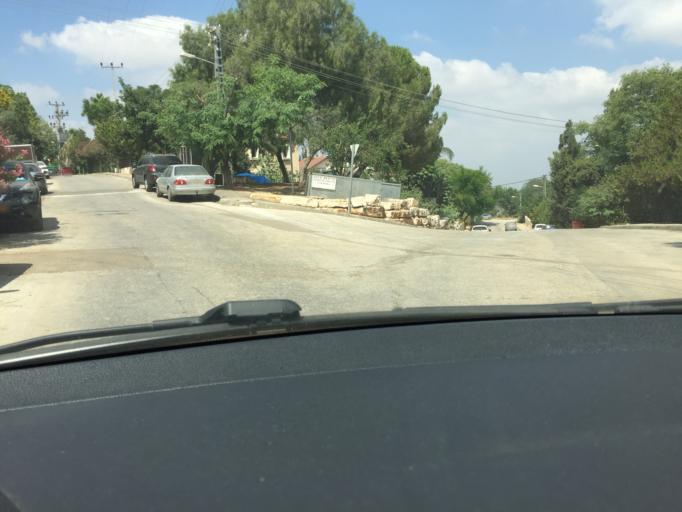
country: PS
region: West Bank
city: Sartah
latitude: 32.1077
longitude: 35.1054
